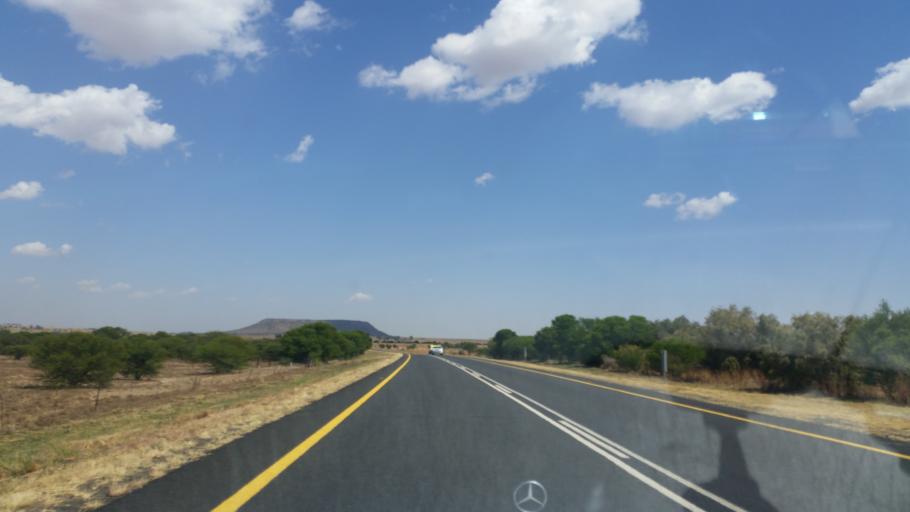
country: ZA
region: Orange Free State
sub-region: Thabo Mofutsanyana District Municipality
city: Senekal
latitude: -28.2971
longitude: 27.7688
